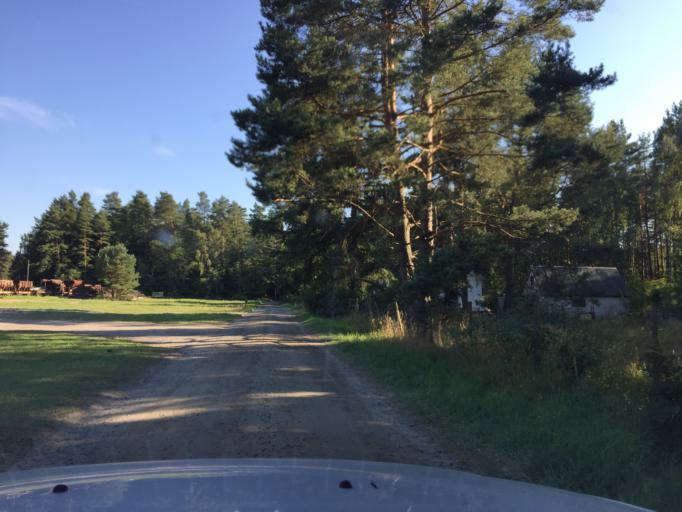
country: SE
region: Skane
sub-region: Kristianstads Kommun
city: Degeberga
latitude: 55.7341
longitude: 14.1247
